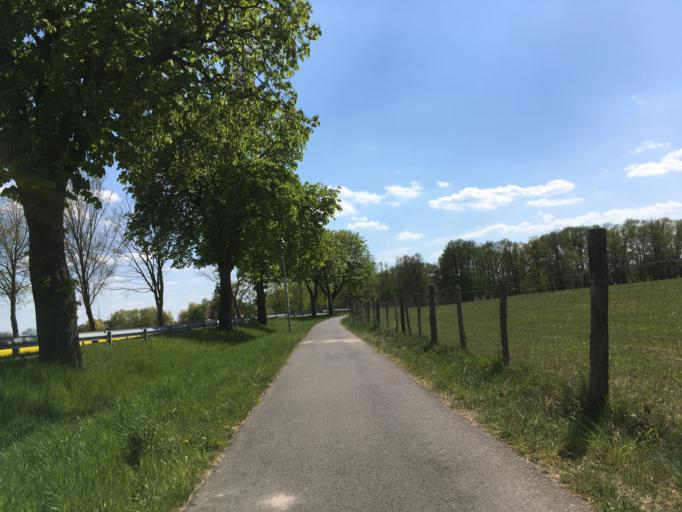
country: DE
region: Brandenburg
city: Werneuchen
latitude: 52.6281
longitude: 13.6825
